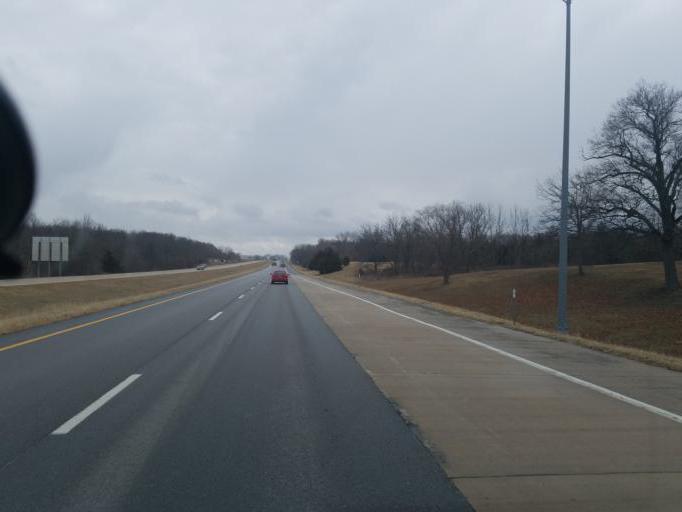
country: US
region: Missouri
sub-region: Randolph County
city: Moberly
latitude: 39.3894
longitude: -92.4134
